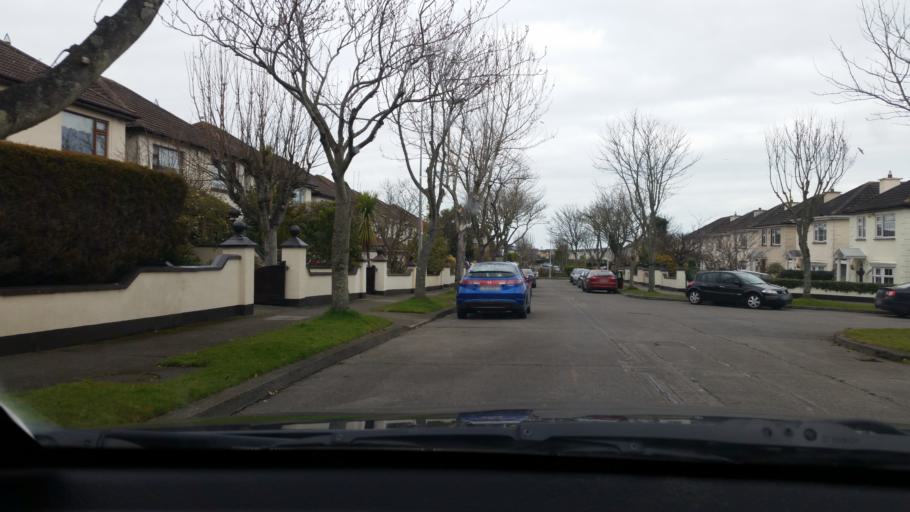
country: IE
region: Leinster
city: Portmarnock
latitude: 53.4300
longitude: -6.1284
